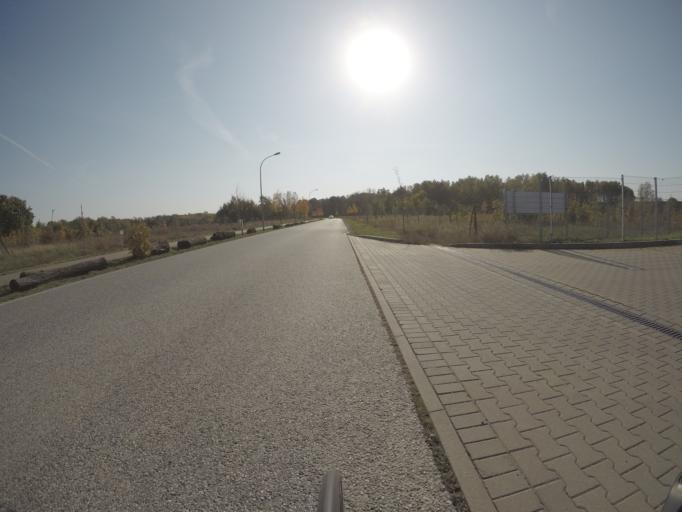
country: DE
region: Brandenburg
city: Leegebruch
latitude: 52.7274
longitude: 13.2225
